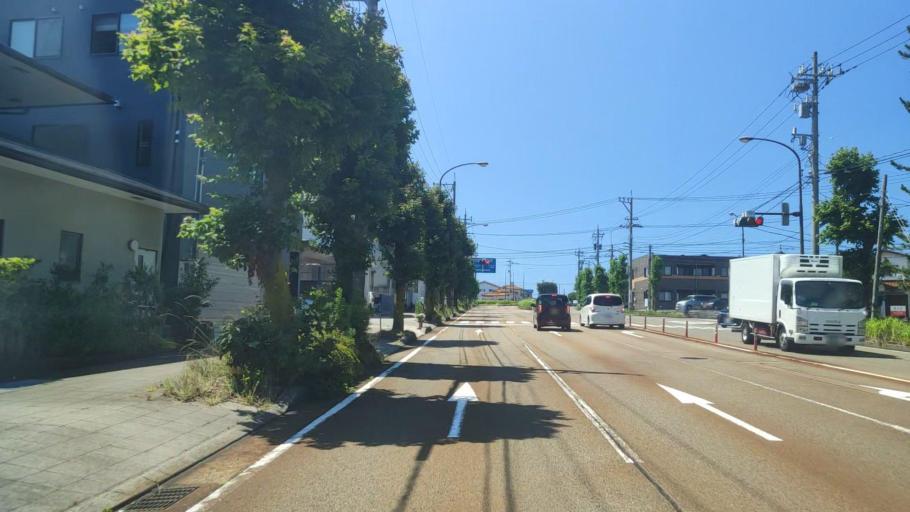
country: JP
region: Ishikawa
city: Kanazawa-shi
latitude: 36.6305
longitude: 136.6287
